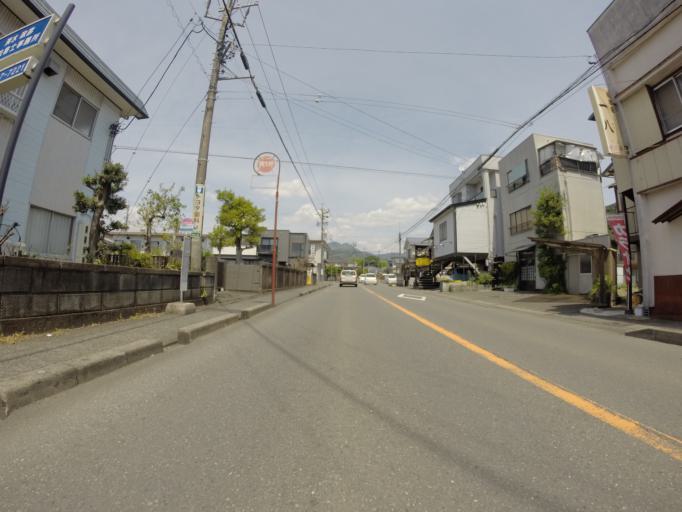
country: JP
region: Shizuoka
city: Shizuoka-shi
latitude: 35.0149
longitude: 138.4232
